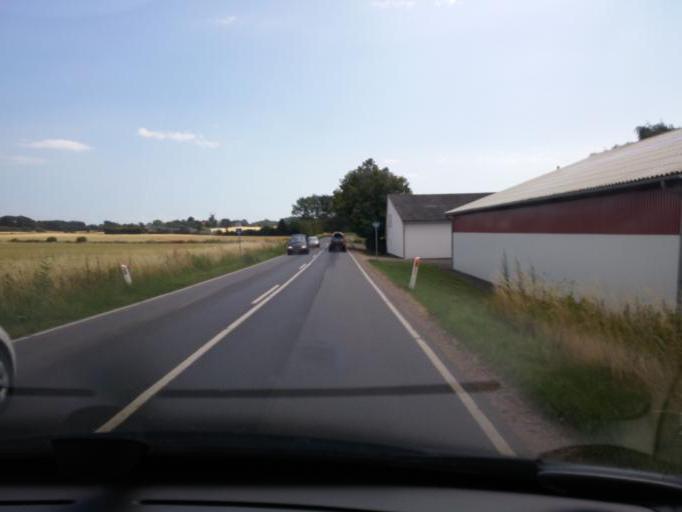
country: DK
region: South Denmark
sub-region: Langeland Kommune
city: Rudkobing
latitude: 54.8764
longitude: 10.7338
